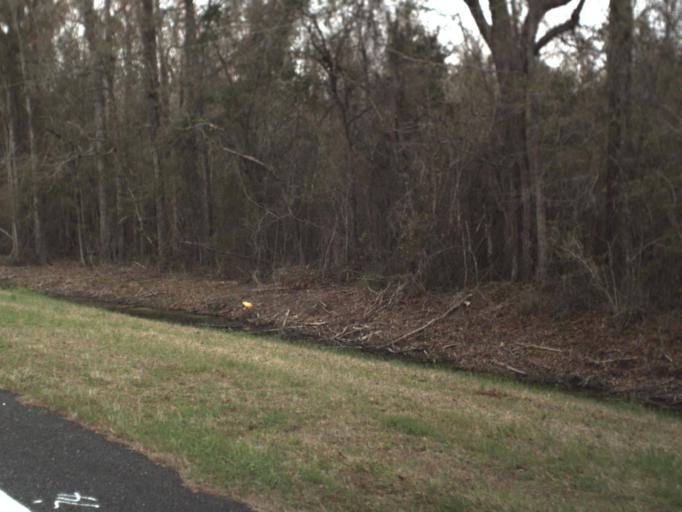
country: US
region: Florida
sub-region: Jefferson County
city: Monticello
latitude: 30.3752
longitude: -83.8110
